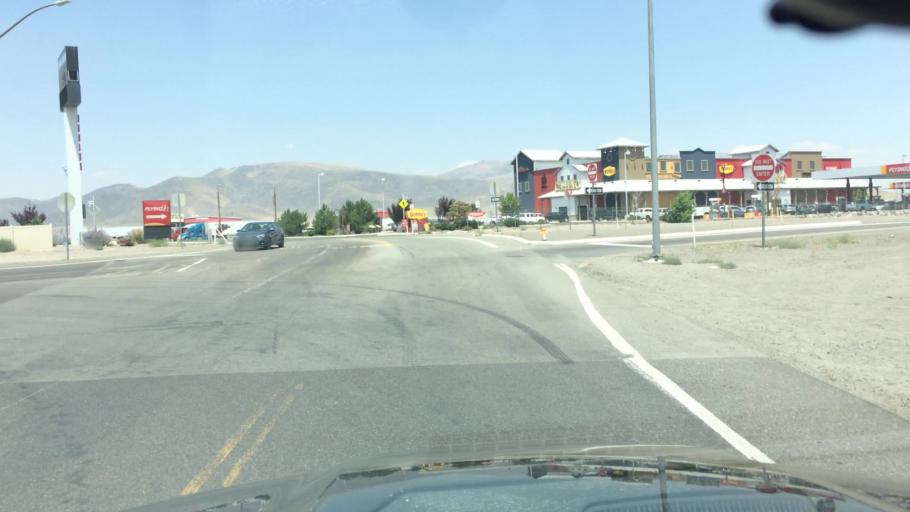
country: US
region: Nevada
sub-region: Lyon County
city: Fernley
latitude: 39.6138
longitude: -119.2179
